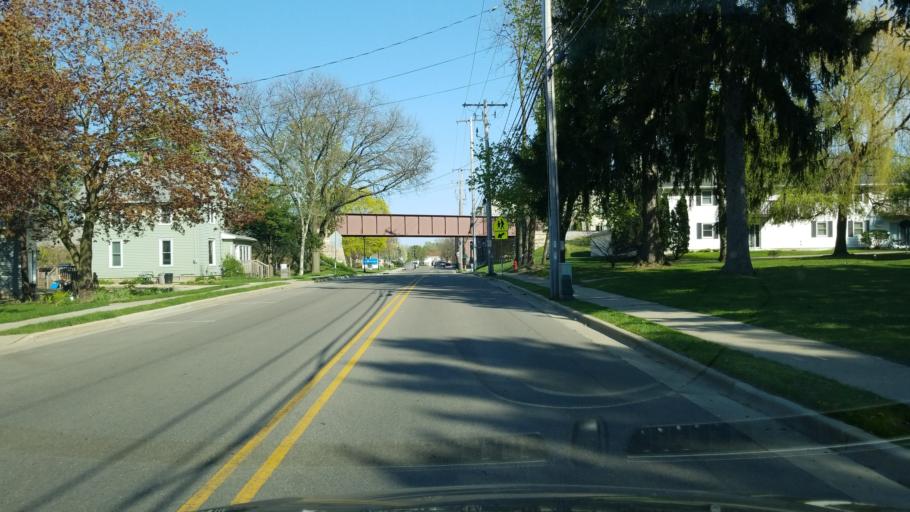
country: US
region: Wisconsin
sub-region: Dane County
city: Oregon
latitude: 42.9272
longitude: -89.3873
